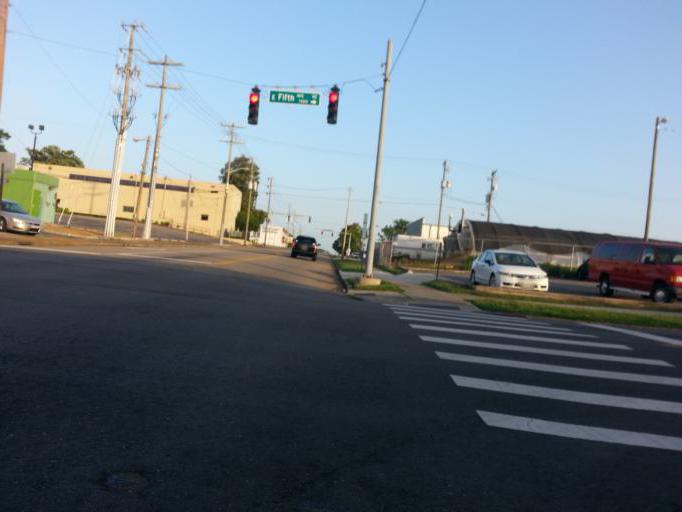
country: US
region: Tennessee
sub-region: Knox County
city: Knoxville
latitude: 35.9790
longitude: -83.9107
